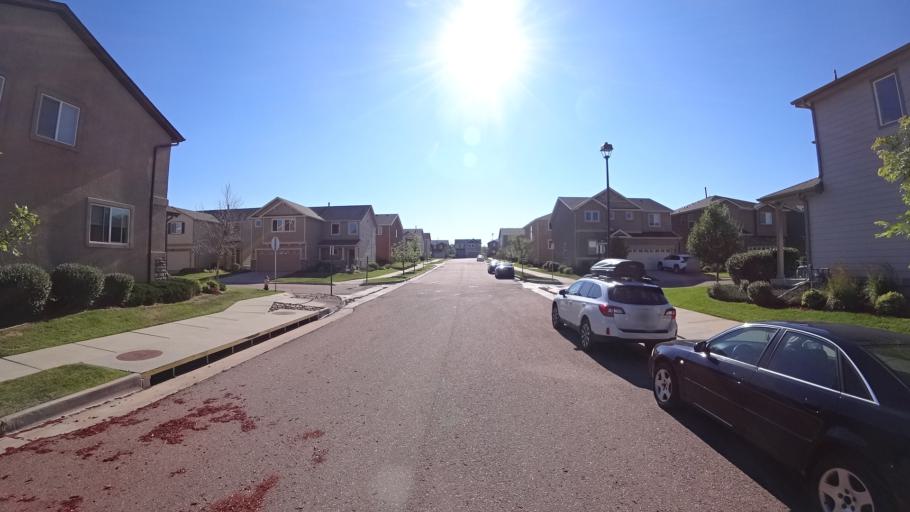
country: US
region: Colorado
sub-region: El Paso County
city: Gleneagle
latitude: 38.9989
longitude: -104.7929
